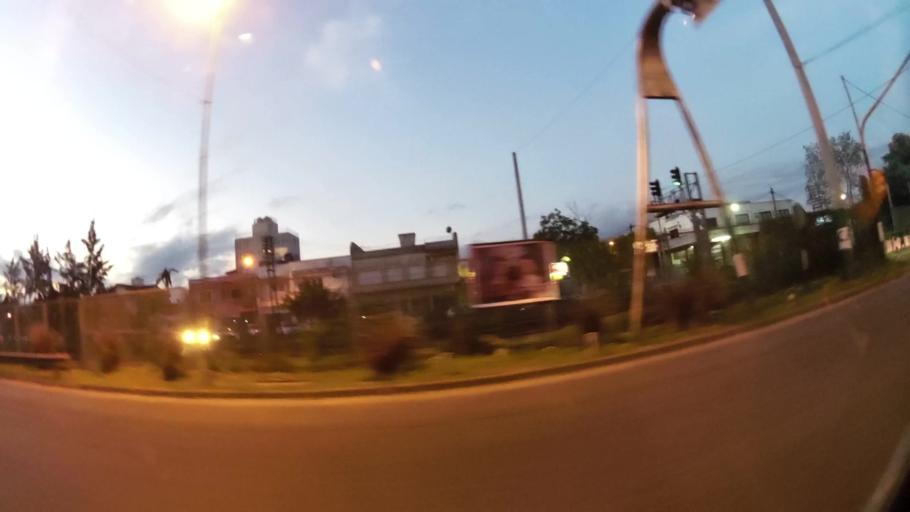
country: AR
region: Buenos Aires
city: Ituzaingo
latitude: -34.6606
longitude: -58.6687
